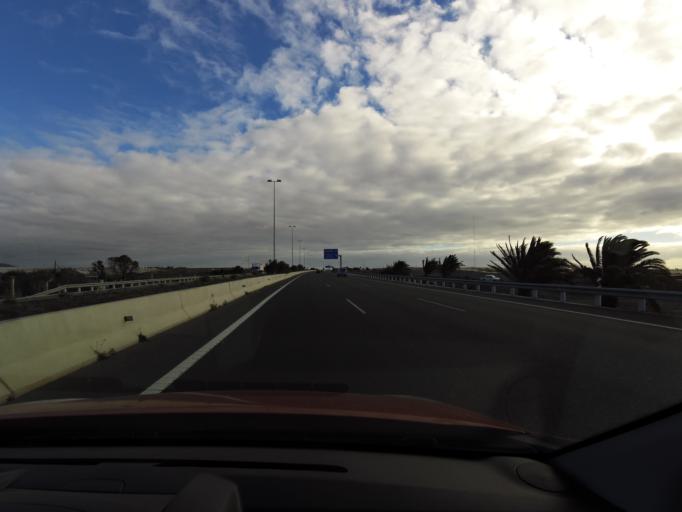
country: ES
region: Canary Islands
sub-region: Provincia de Las Palmas
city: Cruce de Arinaga
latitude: 27.8183
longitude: -15.4682
